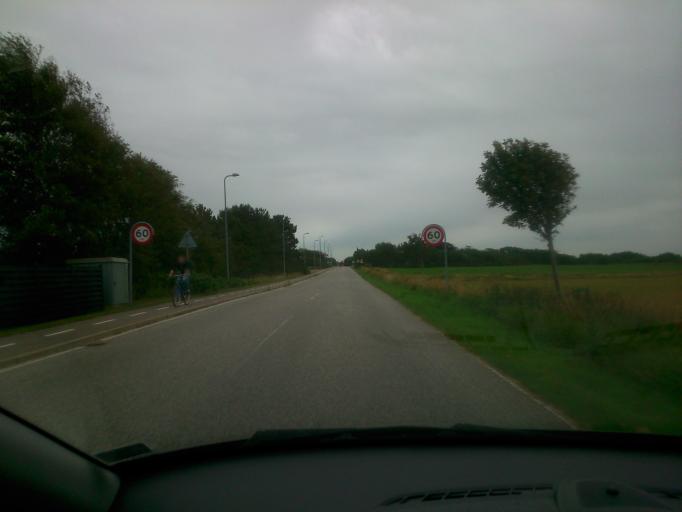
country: DK
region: Central Jutland
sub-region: Ringkobing-Skjern Kommune
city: Skjern
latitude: 55.9580
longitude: 8.4824
